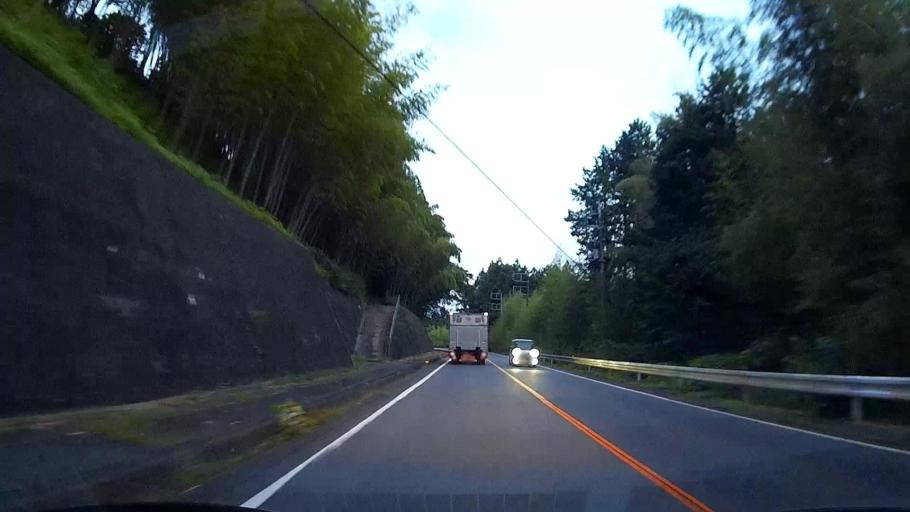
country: JP
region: Gunma
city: Annaka
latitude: 36.3894
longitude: 138.8472
